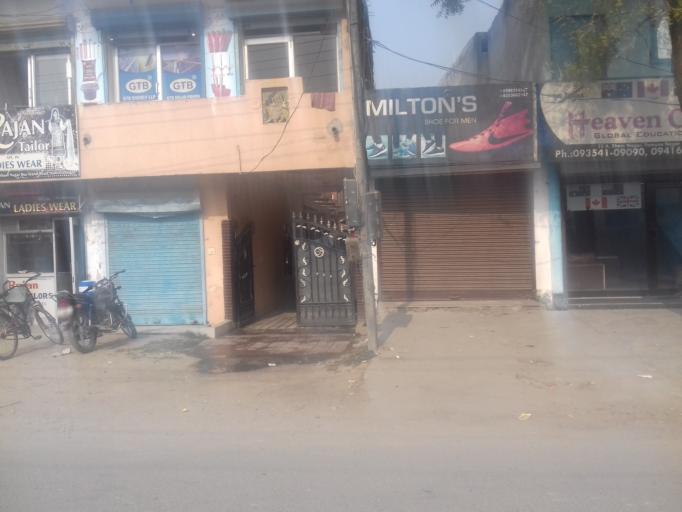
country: IN
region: Haryana
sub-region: Yamunanagar
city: Yamunanagar
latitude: 30.1361
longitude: 77.2795
